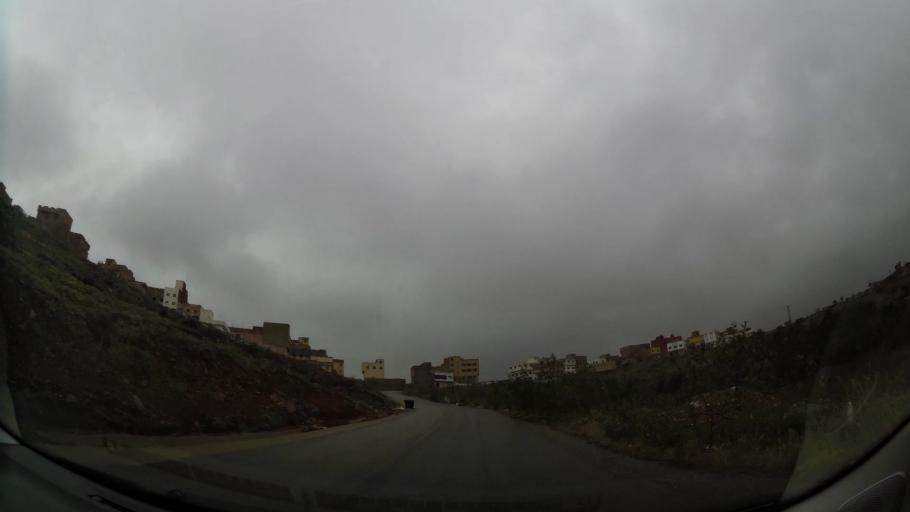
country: MA
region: Oriental
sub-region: Nador
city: Nador
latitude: 35.1864
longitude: -2.9365
